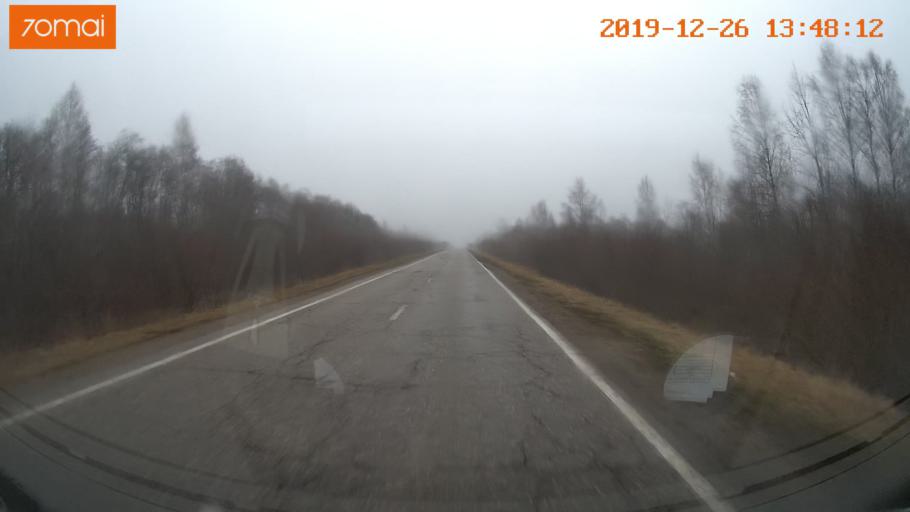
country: RU
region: Vologda
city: Sheksna
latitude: 58.6780
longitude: 38.5445
